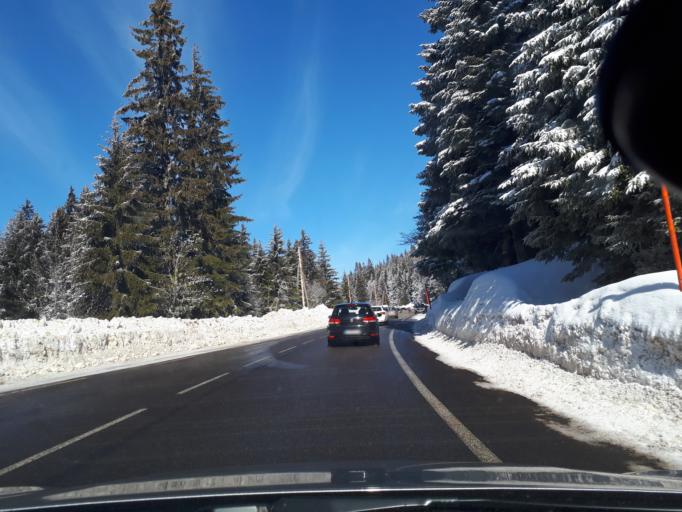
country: FR
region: Rhone-Alpes
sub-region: Departement de l'Isere
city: Vaulnaveys-le-Bas
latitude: 45.1011
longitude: 5.8704
